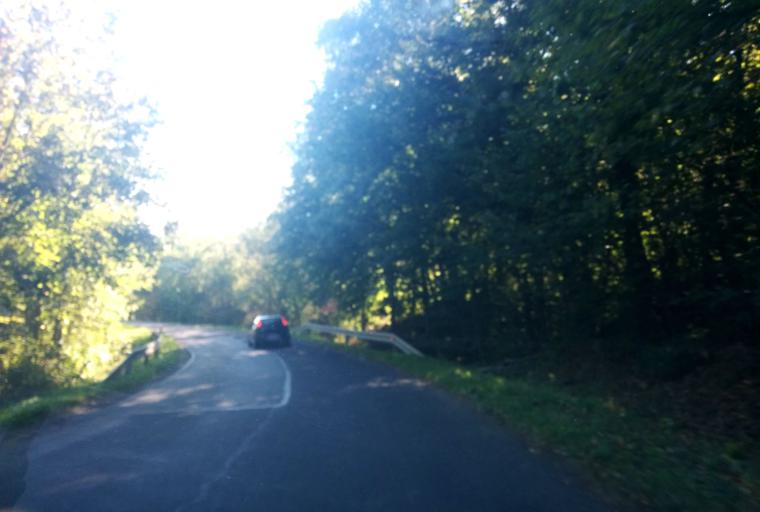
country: PL
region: Subcarpathian Voivodeship
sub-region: Powiat leski
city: Polanczyk
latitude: 49.3256
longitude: 22.4159
